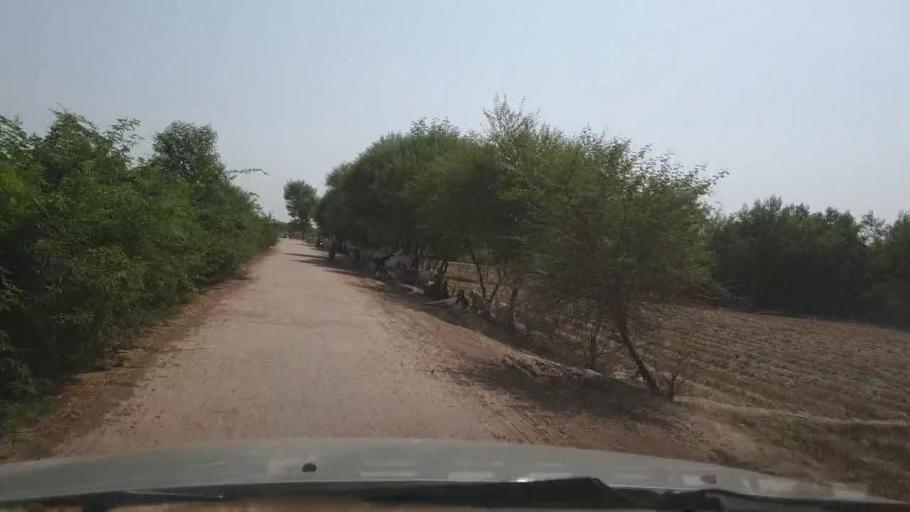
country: PK
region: Sindh
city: Tando Ghulam Ali
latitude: 25.1558
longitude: 68.8950
